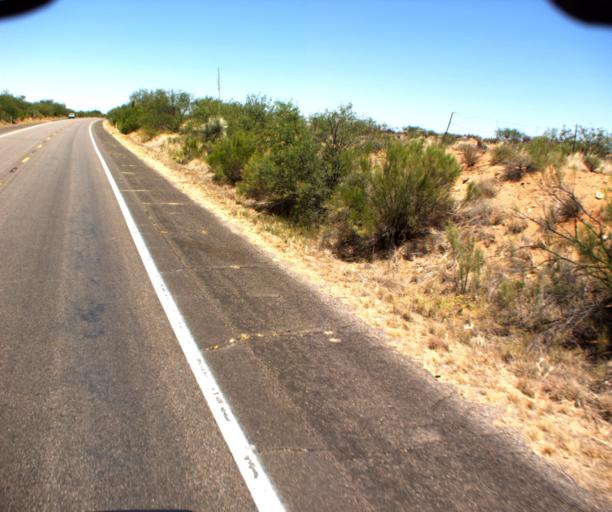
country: US
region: Arizona
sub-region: Pima County
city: Catalina
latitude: 32.5656
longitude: -110.9413
